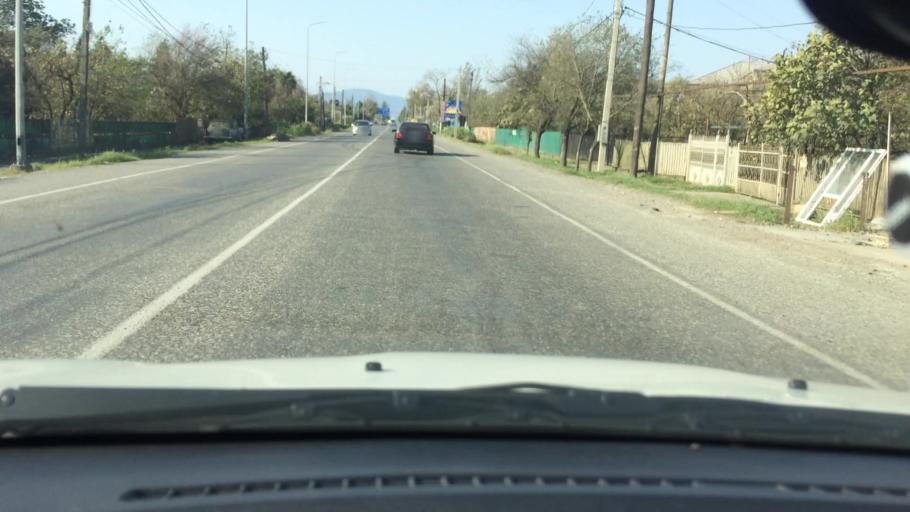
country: GE
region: Imereti
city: Samtredia
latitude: 42.1622
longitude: 42.3530
